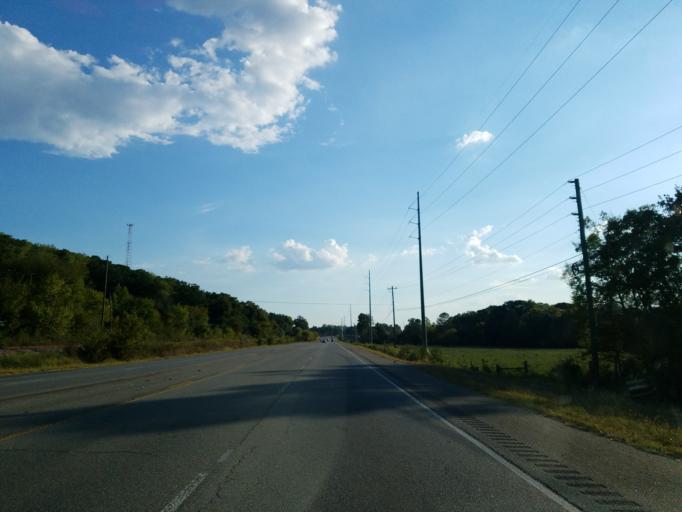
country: US
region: Georgia
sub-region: Murray County
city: Chatsworth
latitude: 34.8089
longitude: -84.7676
